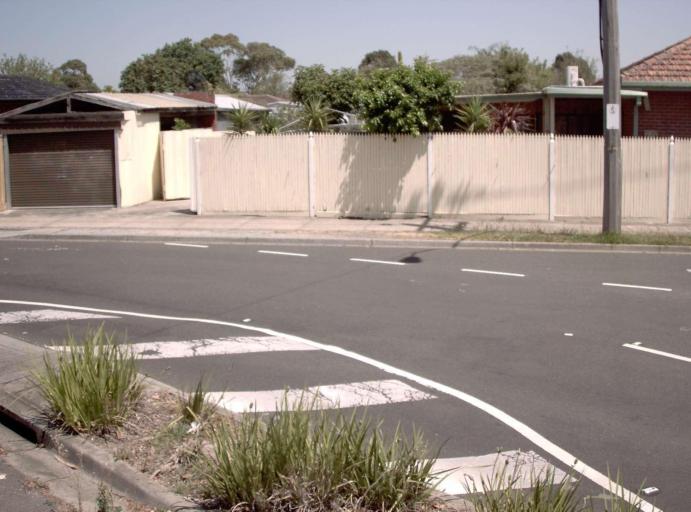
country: AU
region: Victoria
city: Hughesdale
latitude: -37.9104
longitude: 145.0897
